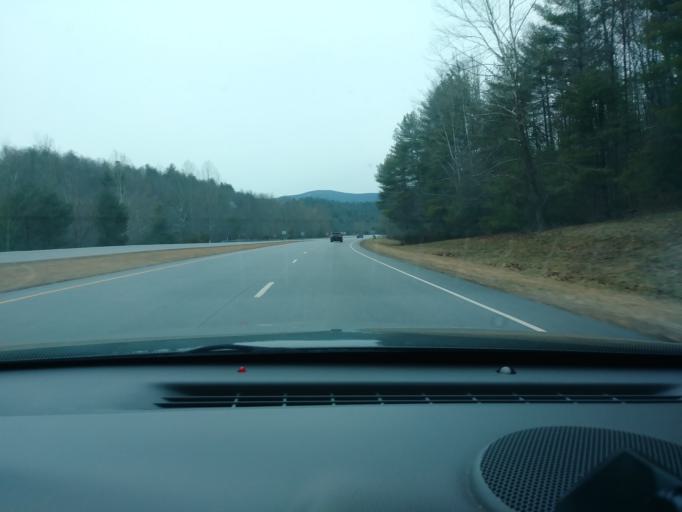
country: US
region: North Carolina
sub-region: Wilkes County
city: Millers Creek
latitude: 36.1878
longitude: -81.4081
